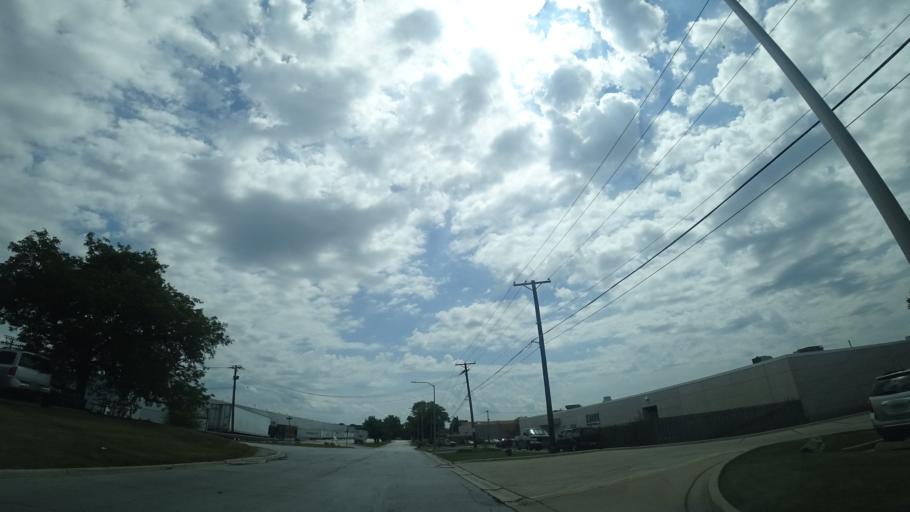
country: US
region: Illinois
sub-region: Cook County
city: Crestwood
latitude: 41.6692
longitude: -87.7487
